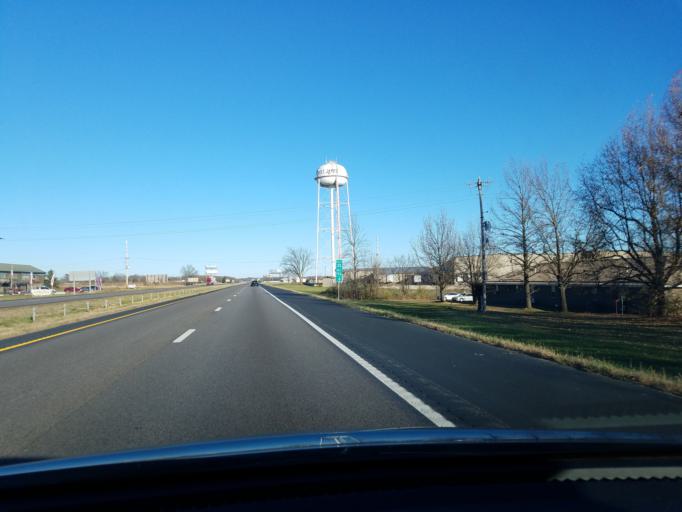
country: US
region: Missouri
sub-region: Phelps County
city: Saint James
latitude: 38.0097
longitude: -91.6054
